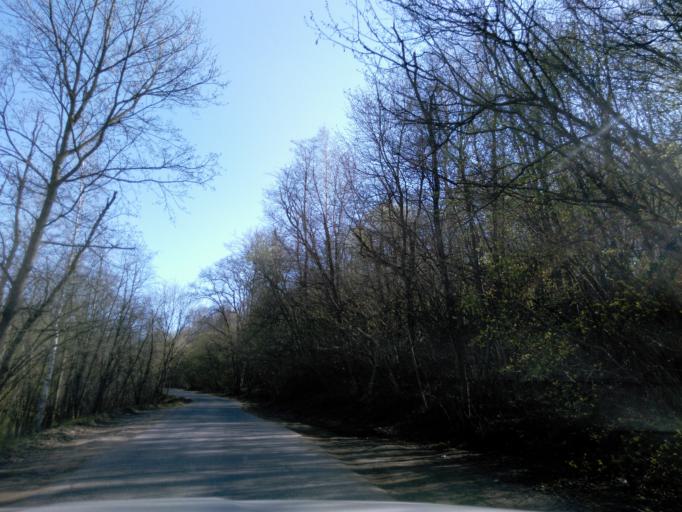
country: RU
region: Moscow
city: Khimki
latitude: 55.8785
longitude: 37.3838
